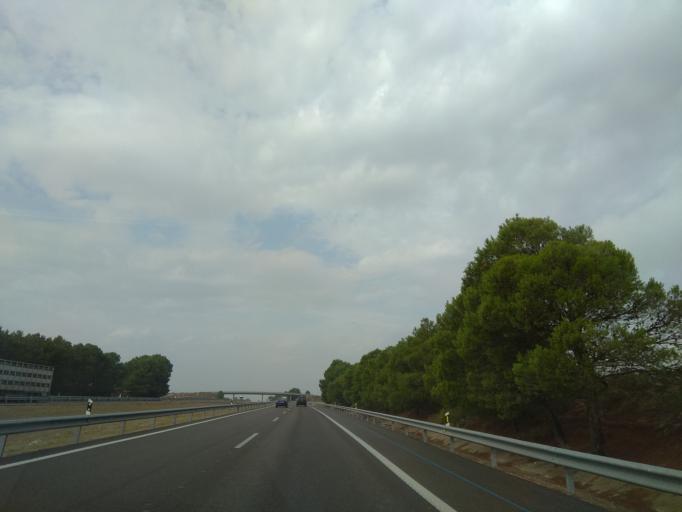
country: ES
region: Aragon
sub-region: Provincia de Zaragoza
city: Bujaraloz
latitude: 41.5189
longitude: -0.2384
